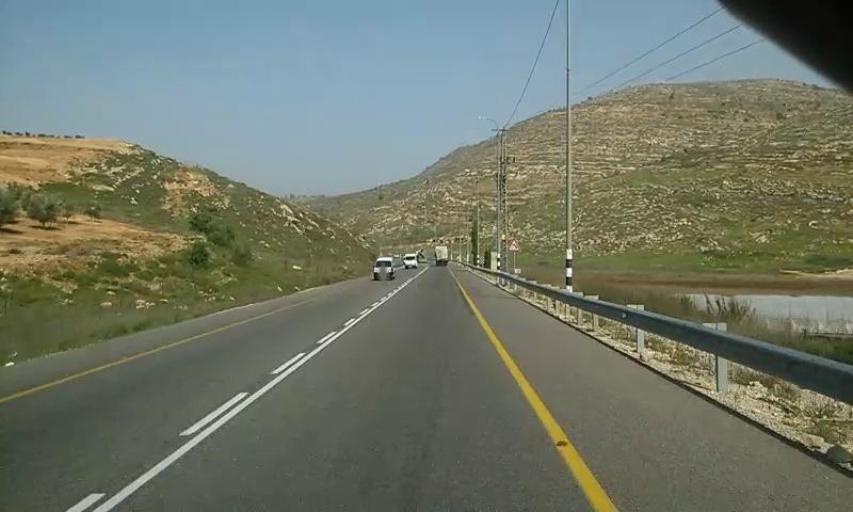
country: PS
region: West Bank
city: Qaryut
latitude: 32.0598
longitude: 35.2823
